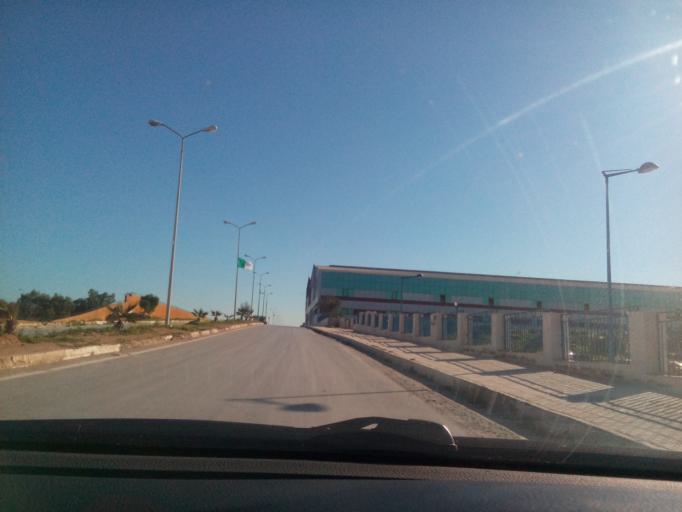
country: DZ
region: Relizane
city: Relizane
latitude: 35.7244
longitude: 0.5262
